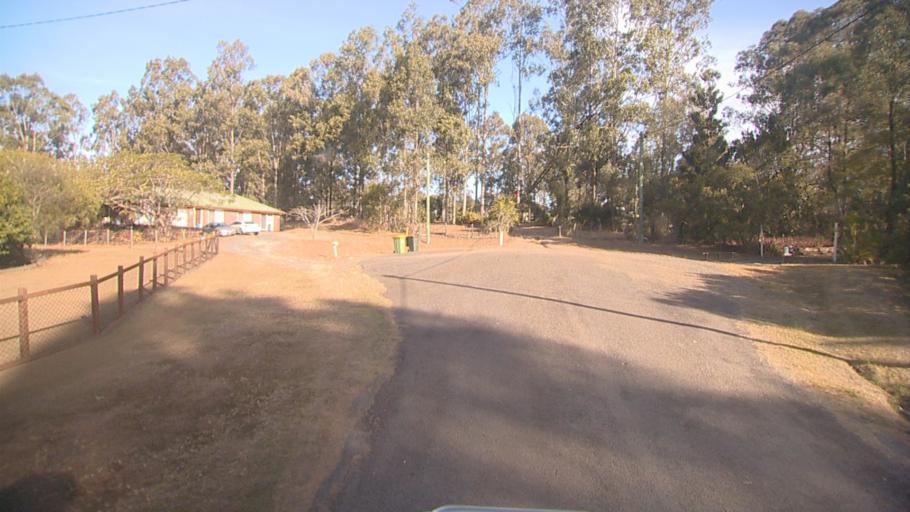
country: AU
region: Queensland
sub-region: Logan
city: Cedar Vale
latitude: -27.8743
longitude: 153.0052
